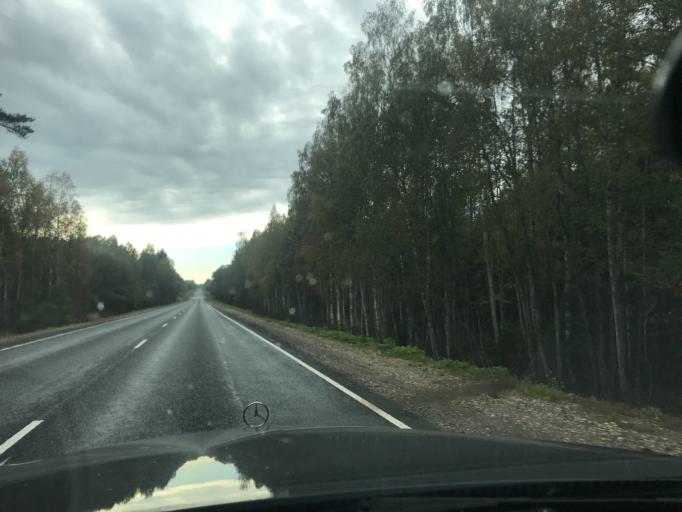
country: RU
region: Pskov
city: Pechory
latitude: 57.6610
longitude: 27.4760
